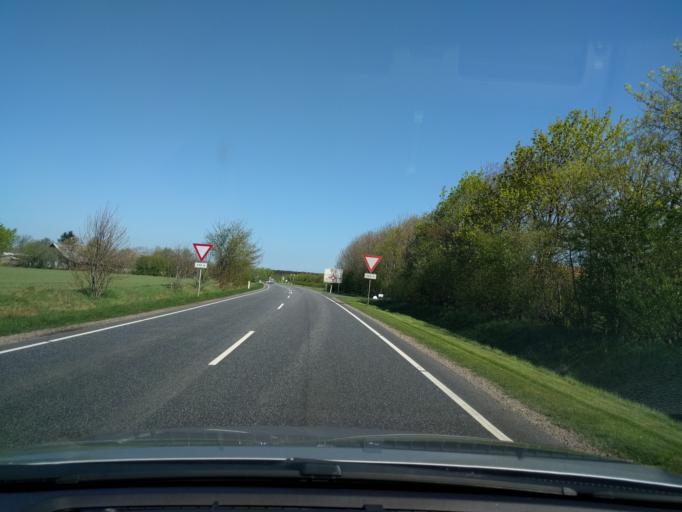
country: DK
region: Central Jutland
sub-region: Ringkobing-Skjern Kommune
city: Videbaek
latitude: 56.0900
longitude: 8.6487
